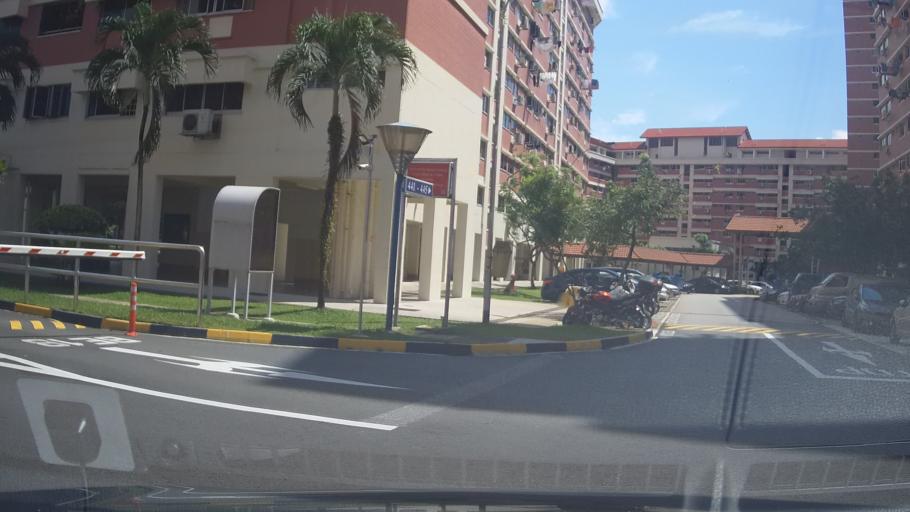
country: SG
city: Singapore
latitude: 1.3588
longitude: 103.8309
